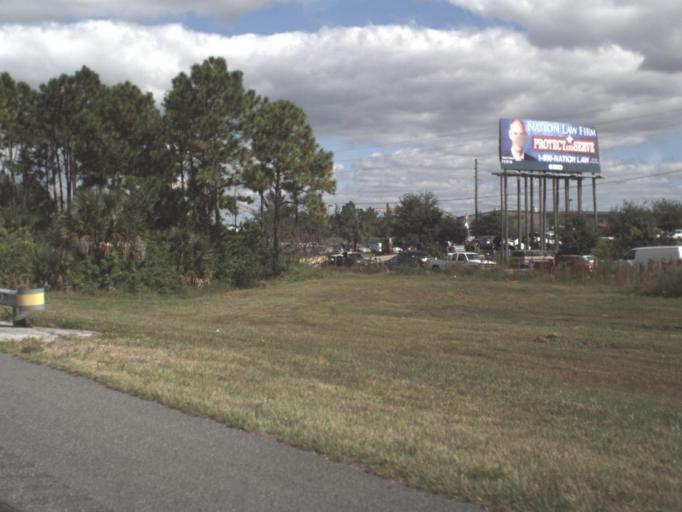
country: US
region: Florida
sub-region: Orange County
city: Southchase
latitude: 28.4027
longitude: -81.3913
